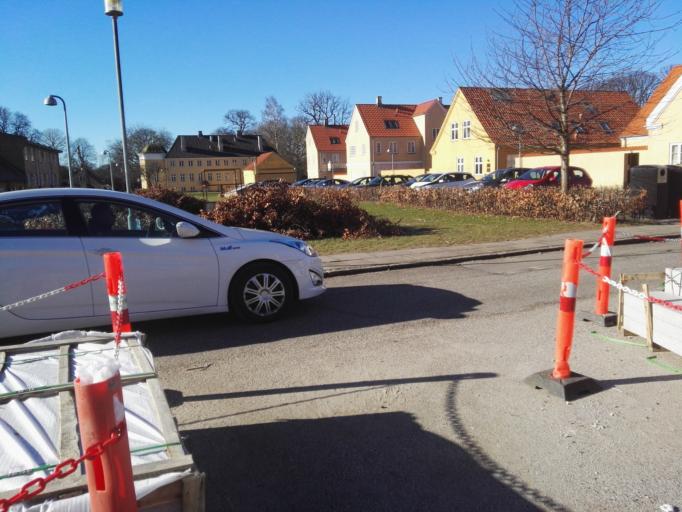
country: DK
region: Capital Region
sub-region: Halsnaes Kommune
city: Frederiksvaerk
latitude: 55.9739
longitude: 12.0200
